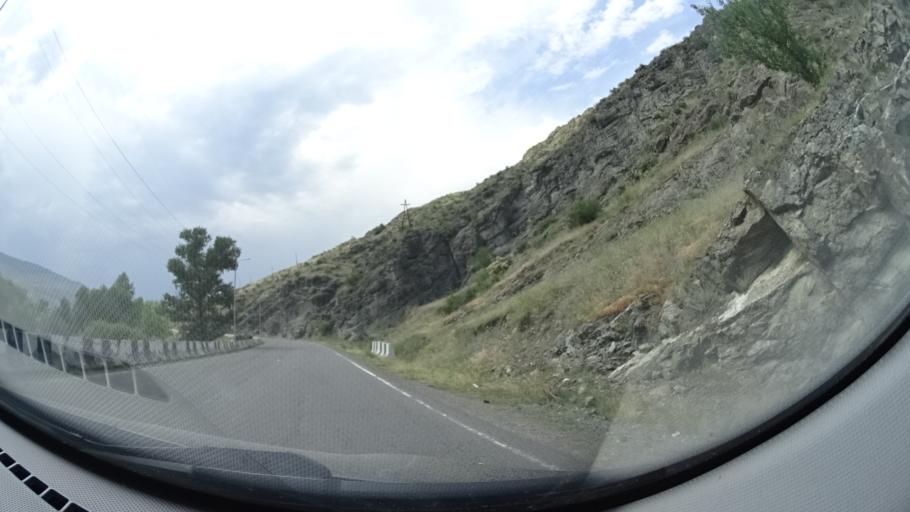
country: GE
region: Samtskhe-Javakheti
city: Aspindza
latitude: 41.5629
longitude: 43.2706
